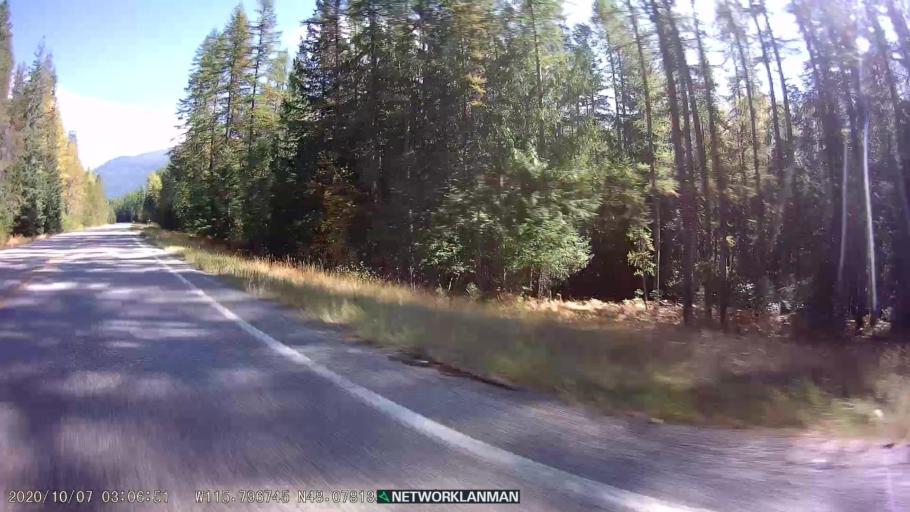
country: US
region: Montana
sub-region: Lincoln County
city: Libby
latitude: 48.0784
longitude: -115.7963
